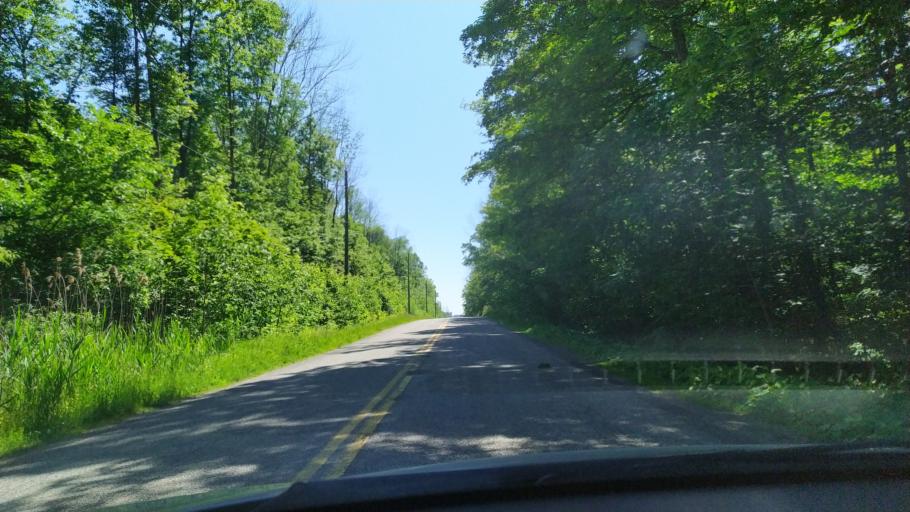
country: CA
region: Ontario
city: Waterloo
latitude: 43.4580
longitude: -80.7238
